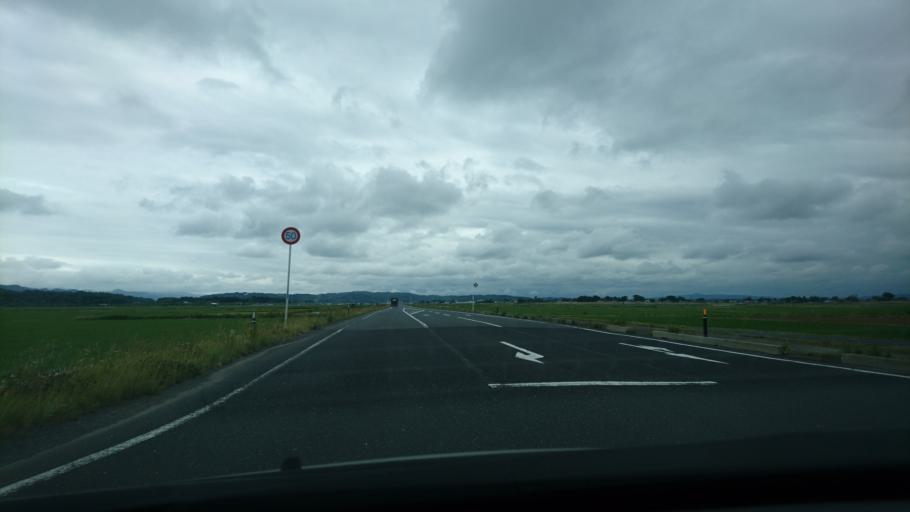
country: JP
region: Miyagi
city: Wakuya
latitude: 38.6899
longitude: 141.2607
